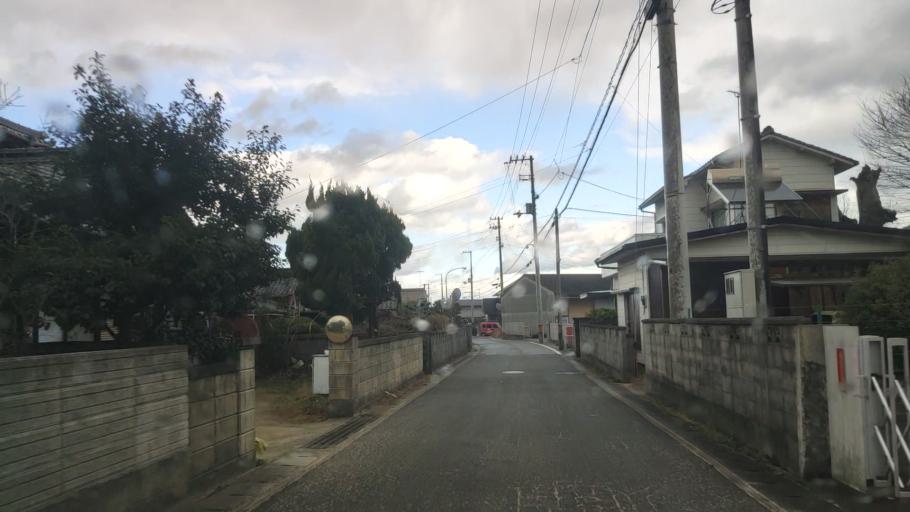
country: JP
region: Tokushima
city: Ishii
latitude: 34.2144
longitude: 134.4145
